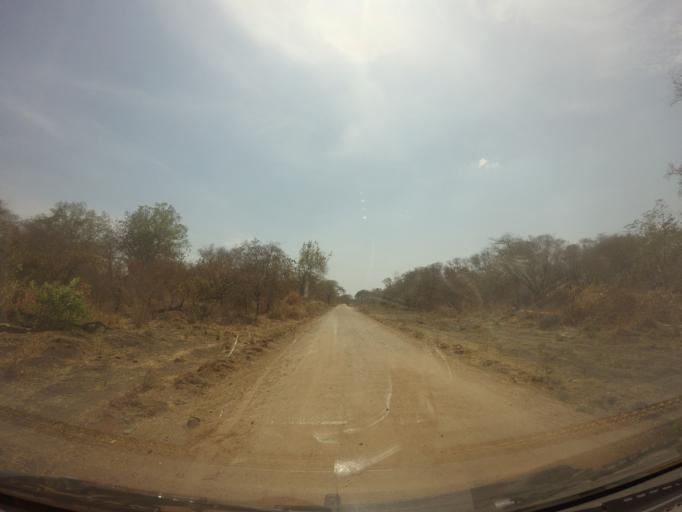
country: UG
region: Northern Region
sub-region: Yumbe District
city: Yumbe
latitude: 3.1904
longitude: 31.2771
